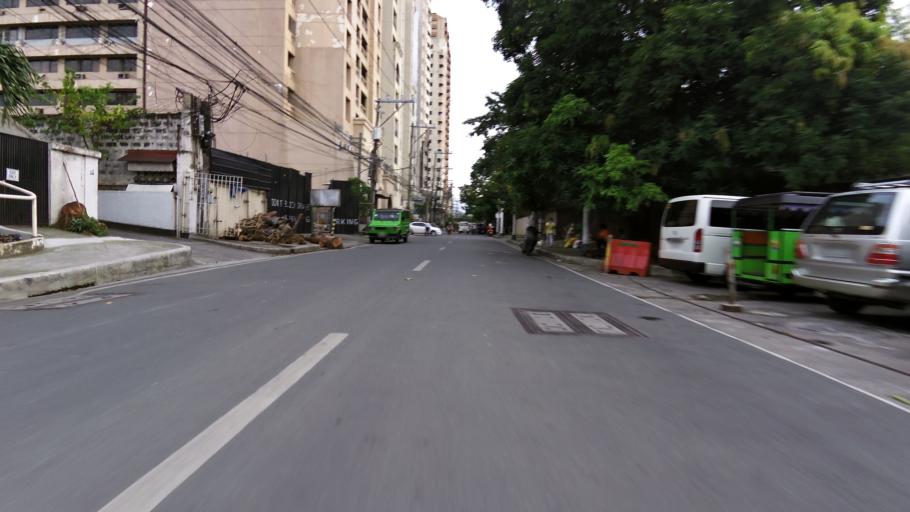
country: PH
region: Metro Manila
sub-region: San Juan
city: San Juan
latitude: 14.6059
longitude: 121.0486
